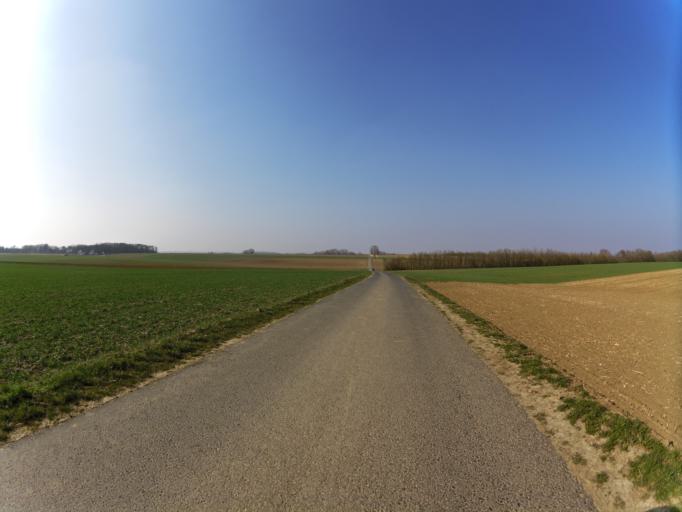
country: DE
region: Bavaria
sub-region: Regierungsbezirk Unterfranken
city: Gaukonigshofen
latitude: 49.6557
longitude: 9.9967
